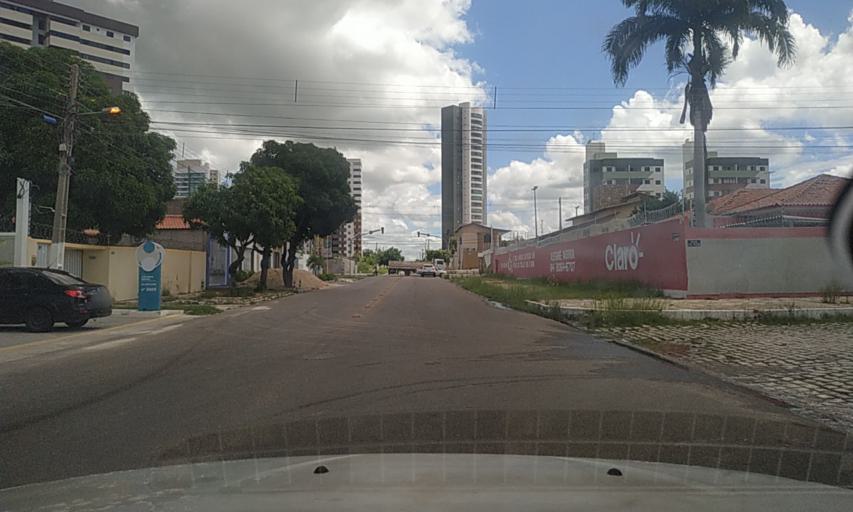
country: BR
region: Rio Grande do Norte
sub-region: Mossoro
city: Mossoro
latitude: -5.1803
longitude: -37.3599
